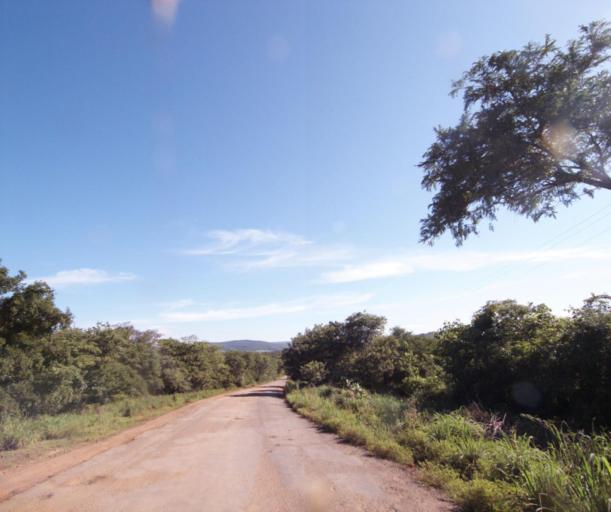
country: BR
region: Bahia
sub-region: Sao Felix Do Coribe
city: Santa Maria da Vitoria
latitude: -13.6475
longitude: -44.4431
